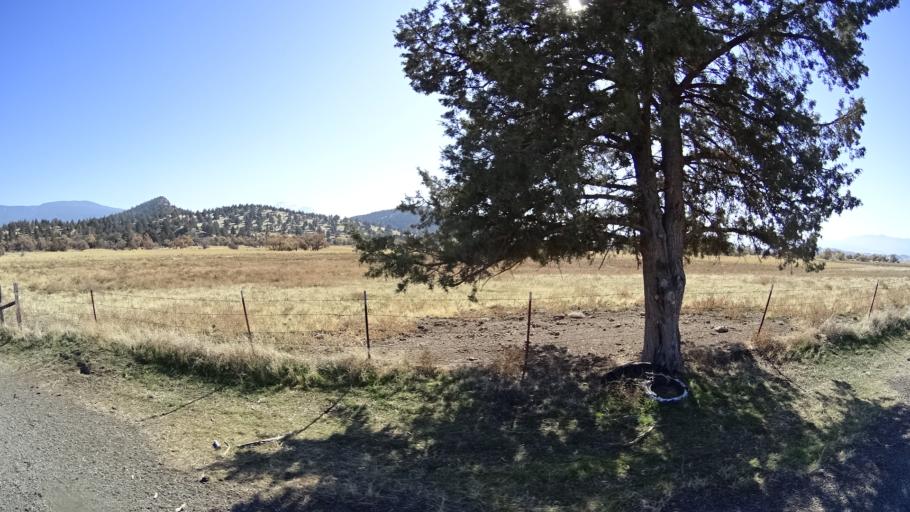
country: US
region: California
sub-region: Siskiyou County
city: Montague
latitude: 41.7263
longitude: -122.3727
